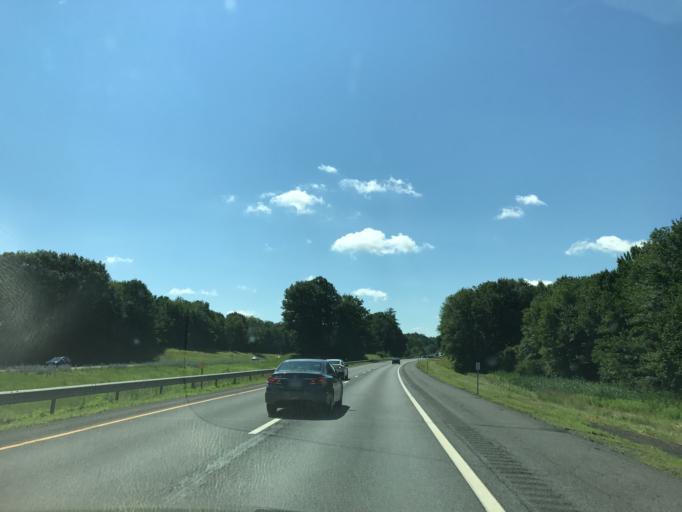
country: US
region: New York
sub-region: Rensselaer County
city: Nassau
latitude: 42.4572
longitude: -73.5808
